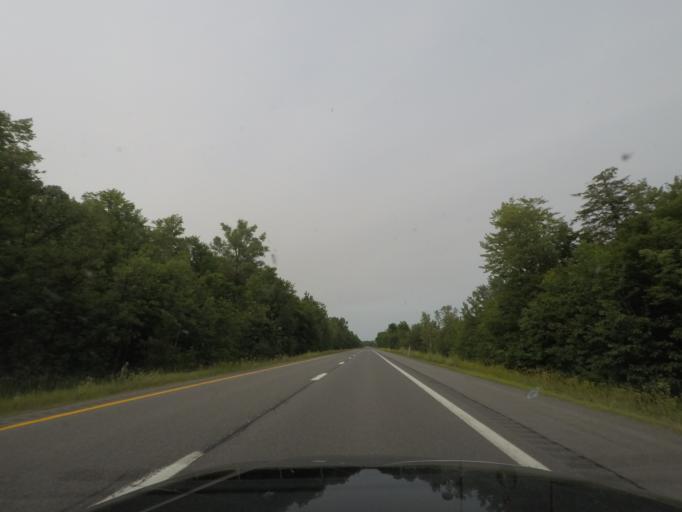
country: US
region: New York
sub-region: Clinton County
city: Champlain
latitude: 44.9044
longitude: -73.4528
